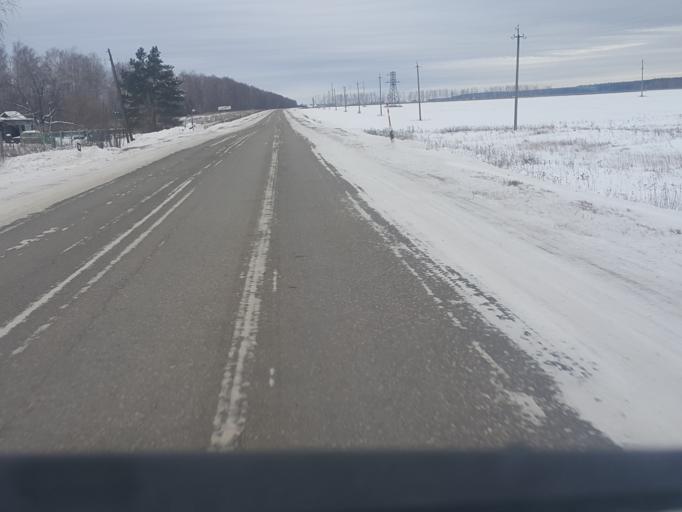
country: RU
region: Tambov
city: Platonovka
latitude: 52.8263
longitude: 41.8037
